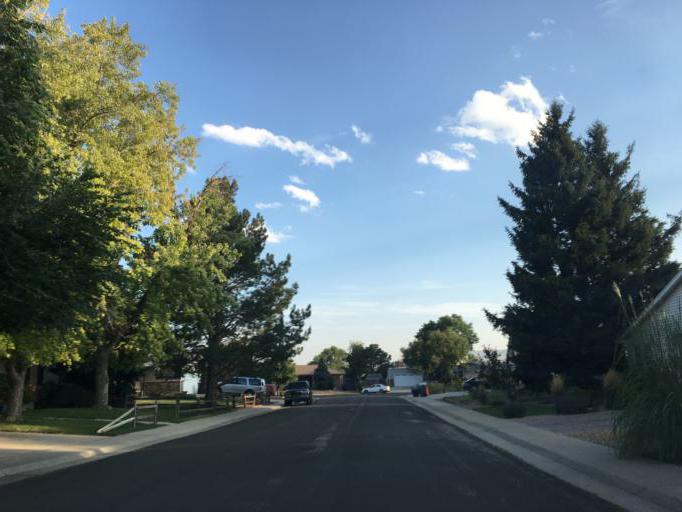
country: US
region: Colorado
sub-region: Jefferson County
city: Applewood
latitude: 39.7902
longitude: -105.1507
